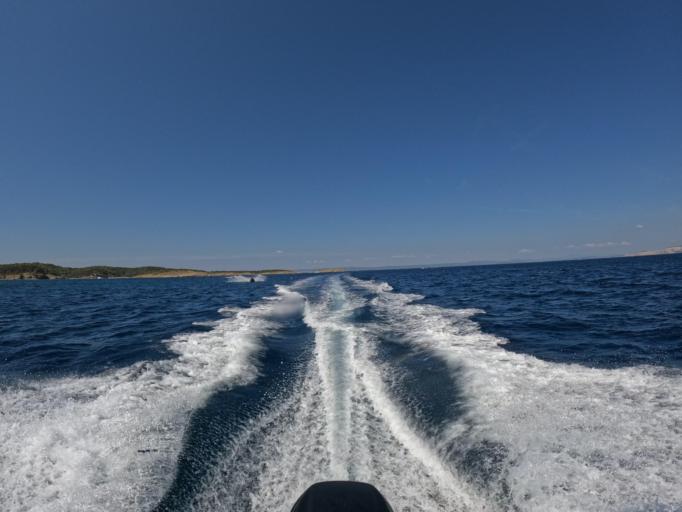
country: HR
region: Primorsko-Goranska
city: Lopar
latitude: 44.8527
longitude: 14.7440
